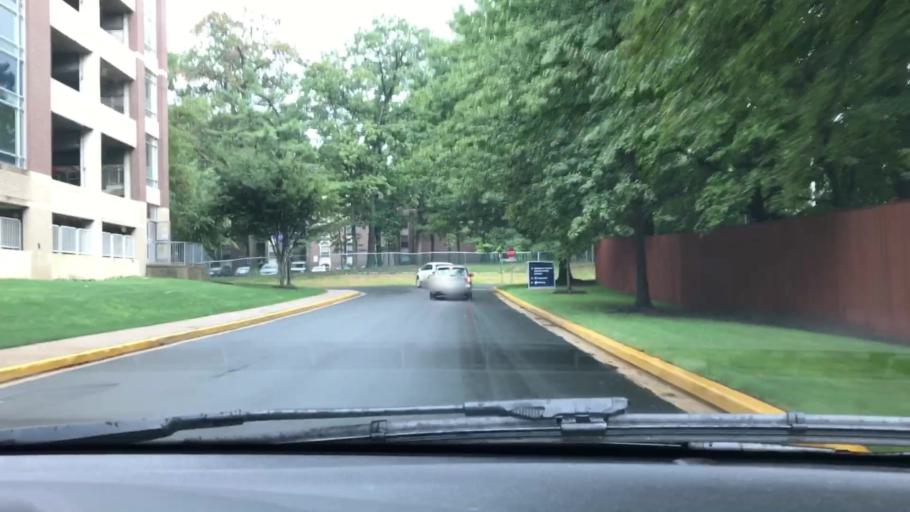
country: US
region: Virginia
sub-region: Fairfax County
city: Merrifield
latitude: 38.8575
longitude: -77.2311
